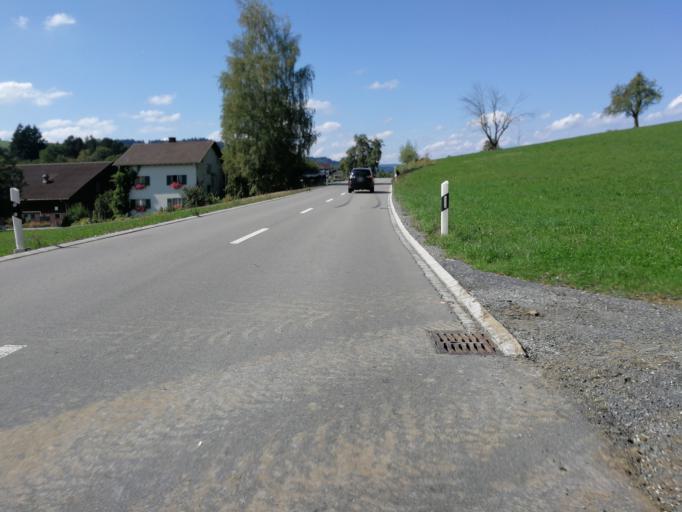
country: CH
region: Zurich
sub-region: Bezirk Horgen
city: Au / Unter-Dorf
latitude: 47.2327
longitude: 8.6304
